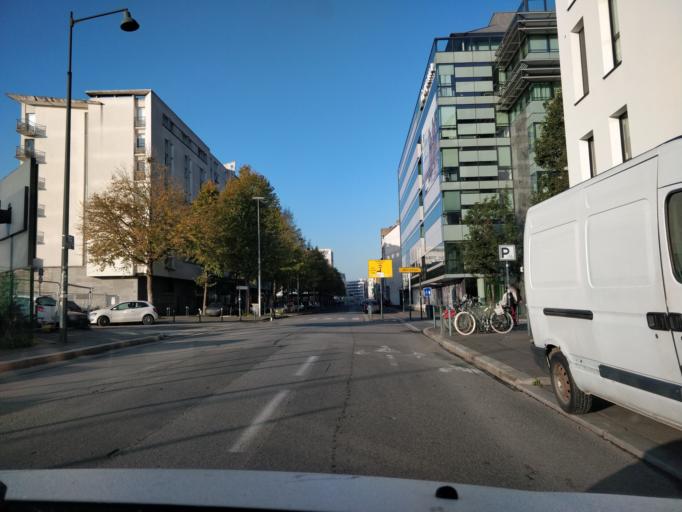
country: FR
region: Brittany
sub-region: Departement d'Ille-et-Vilaine
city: Rennes
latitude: 48.1046
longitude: -1.6682
